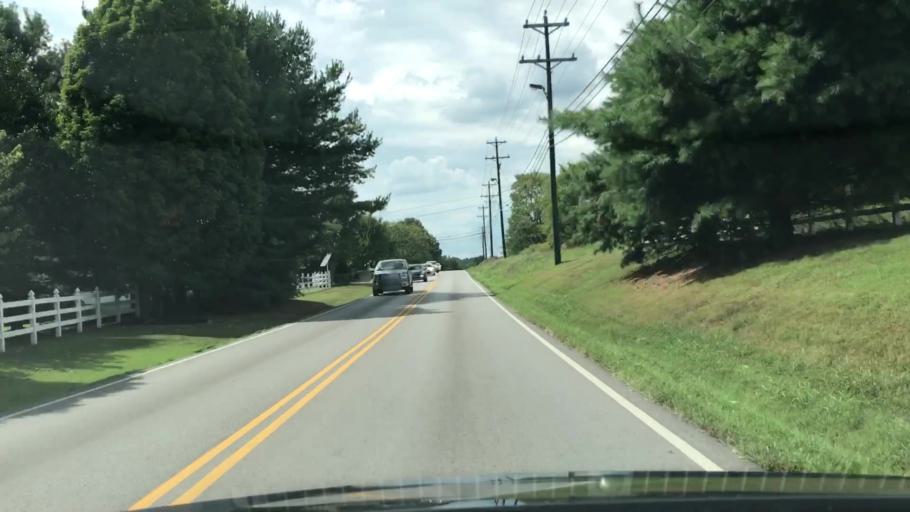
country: US
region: Tennessee
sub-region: Williamson County
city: Thompson's Station
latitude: 35.7824
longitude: -86.8997
